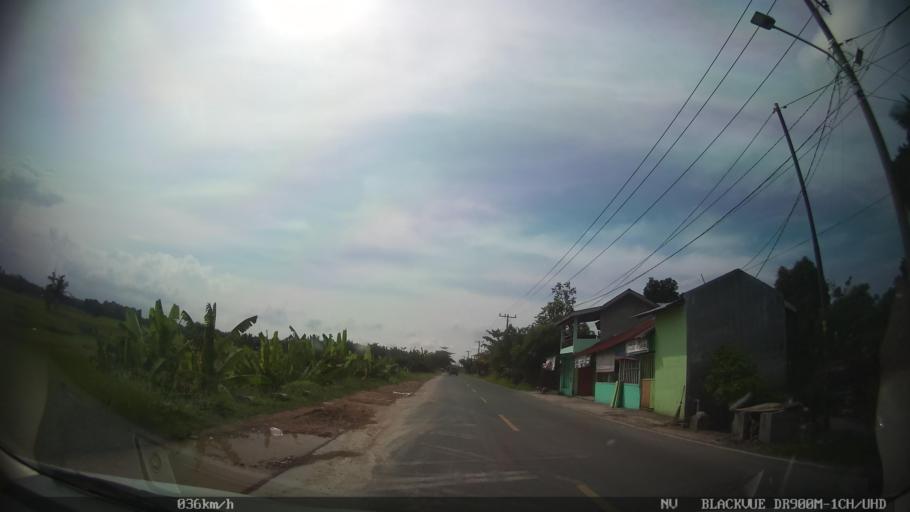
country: ID
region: North Sumatra
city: Percut
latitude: 3.6118
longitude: 98.8459
